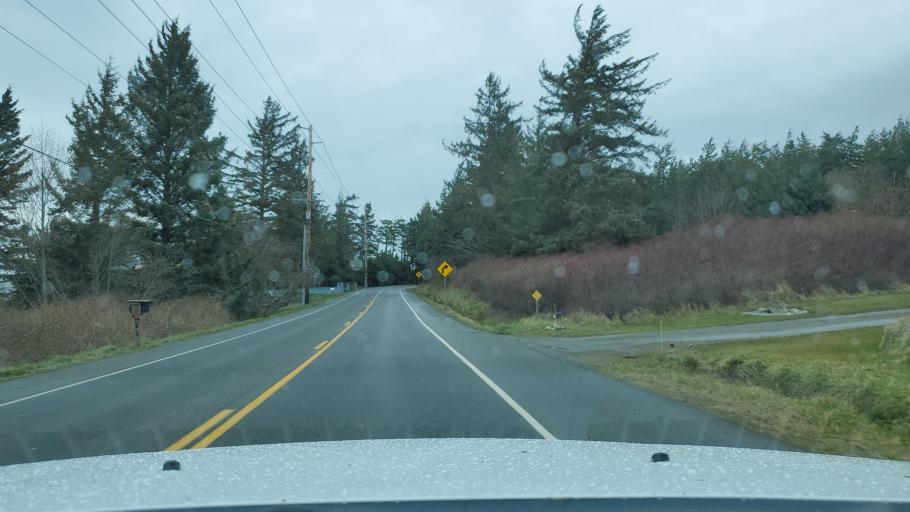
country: US
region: Washington
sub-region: Island County
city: Coupeville
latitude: 48.2594
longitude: -122.7509
